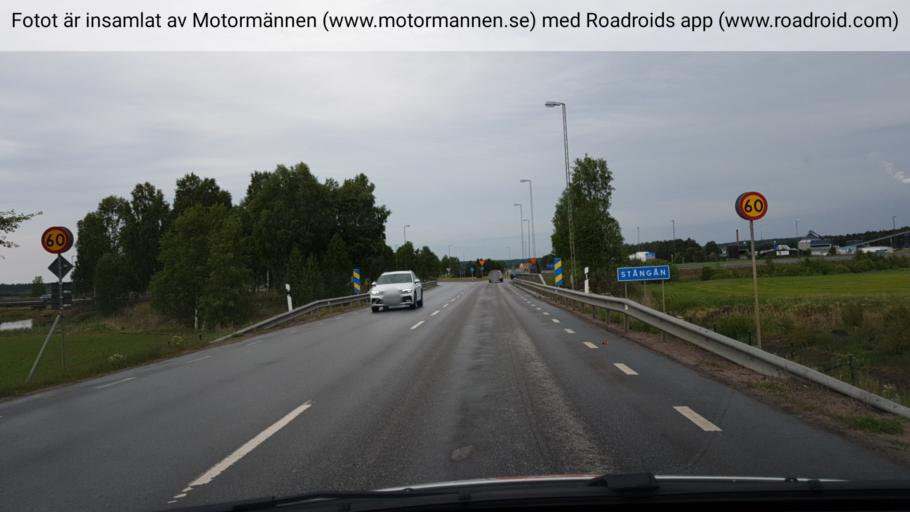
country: SE
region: Kalmar
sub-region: Vimmerby Kommun
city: Vimmerby
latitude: 57.6494
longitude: 15.8387
